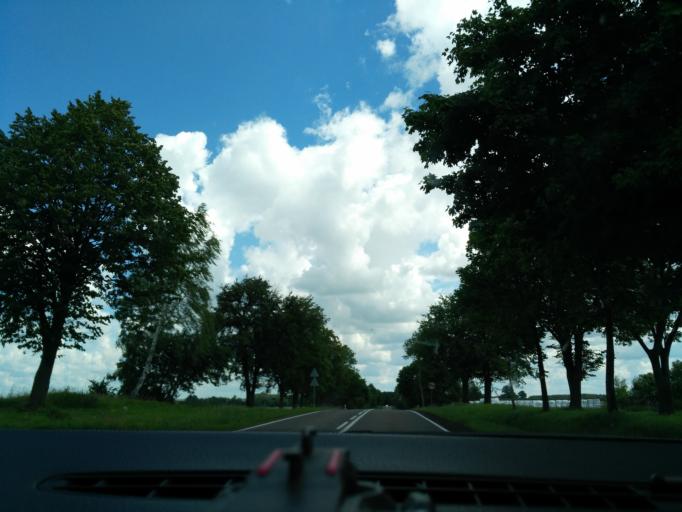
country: PL
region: Podlasie
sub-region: Powiat siemiatycki
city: Dziadkowice
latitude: 52.6003
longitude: 22.9695
